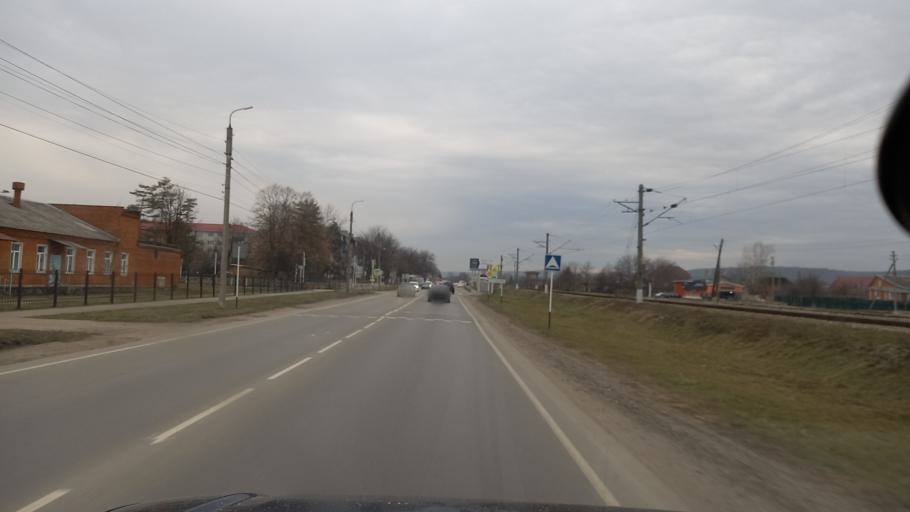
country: RU
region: Adygeya
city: Maykop
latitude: 44.5973
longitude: 40.1326
